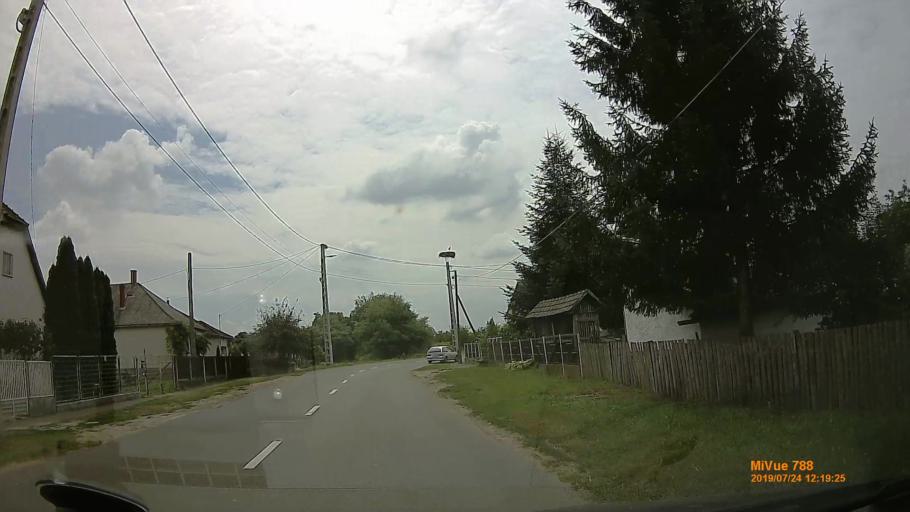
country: HU
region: Szabolcs-Szatmar-Bereg
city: Vasarosnameny
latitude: 48.1410
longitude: 22.3454
